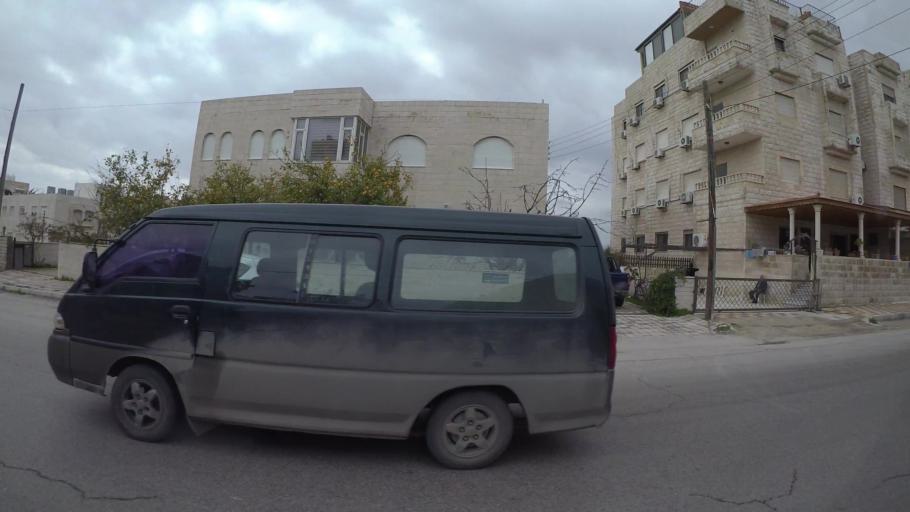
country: JO
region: Amman
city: Wadi as Sir
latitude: 31.9608
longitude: 35.8352
